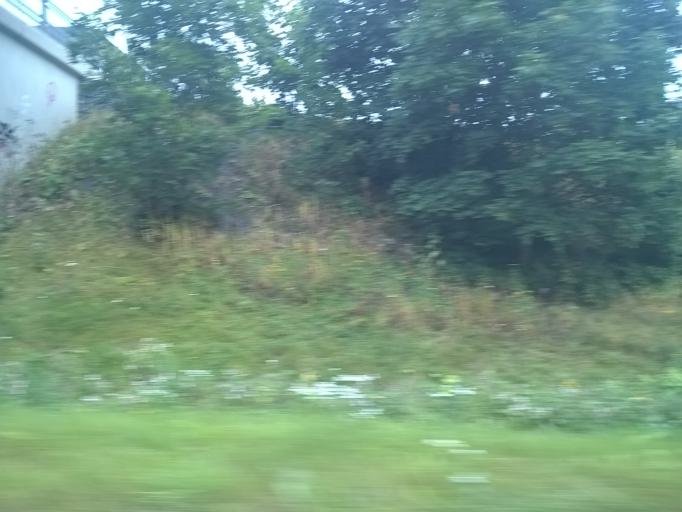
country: FI
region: Pirkanmaa
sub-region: Tampere
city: Tampere
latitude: 61.4554
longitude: 23.8479
